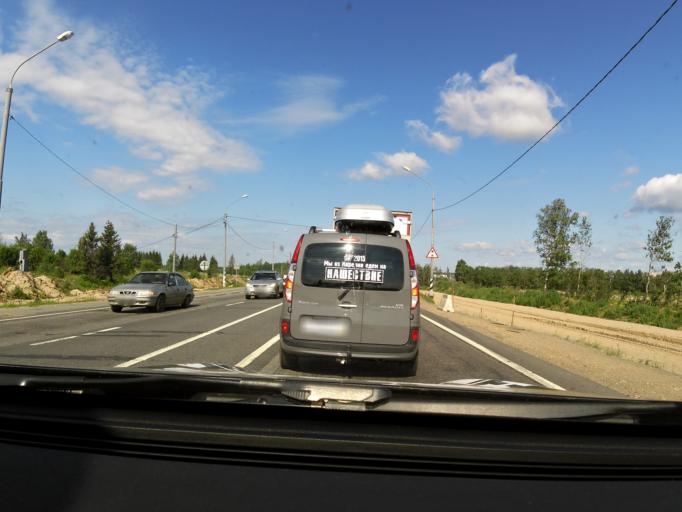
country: RU
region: Tverskaya
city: Tver
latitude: 56.7876
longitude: 35.9189
